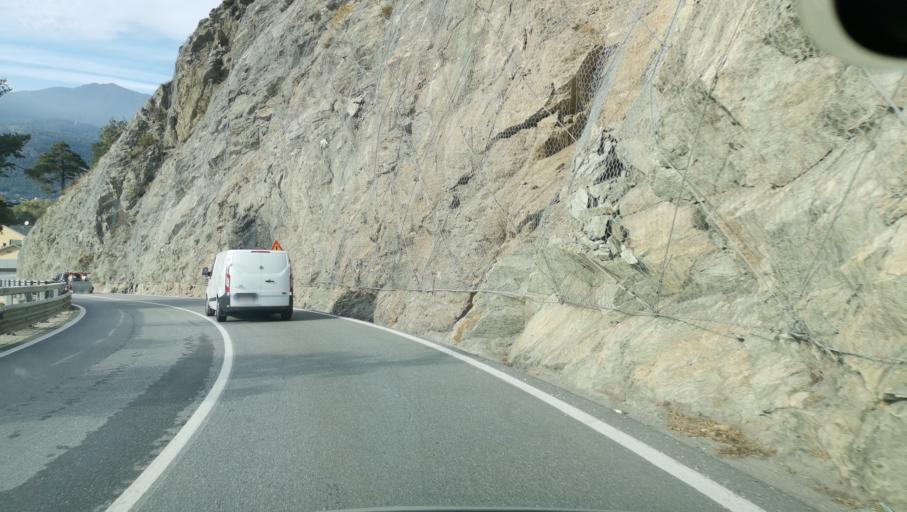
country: IT
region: Piedmont
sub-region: Provincia di Torino
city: Oulx
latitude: 45.0502
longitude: 6.8491
